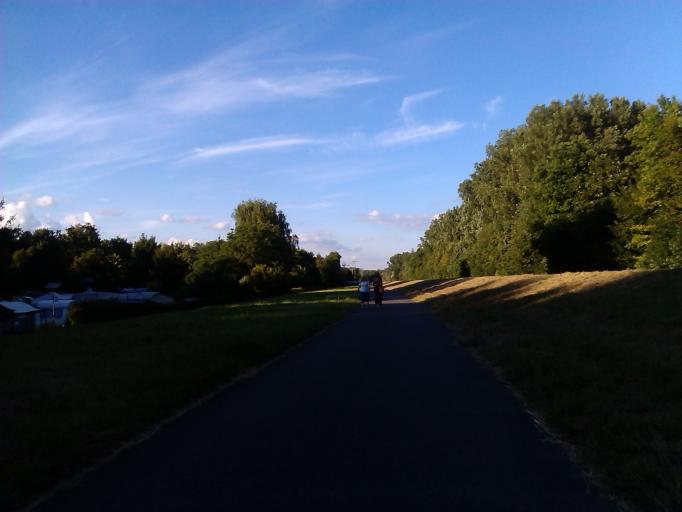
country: DE
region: Rheinland-Pfalz
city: Altrip
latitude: 49.3994
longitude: 8.4825
